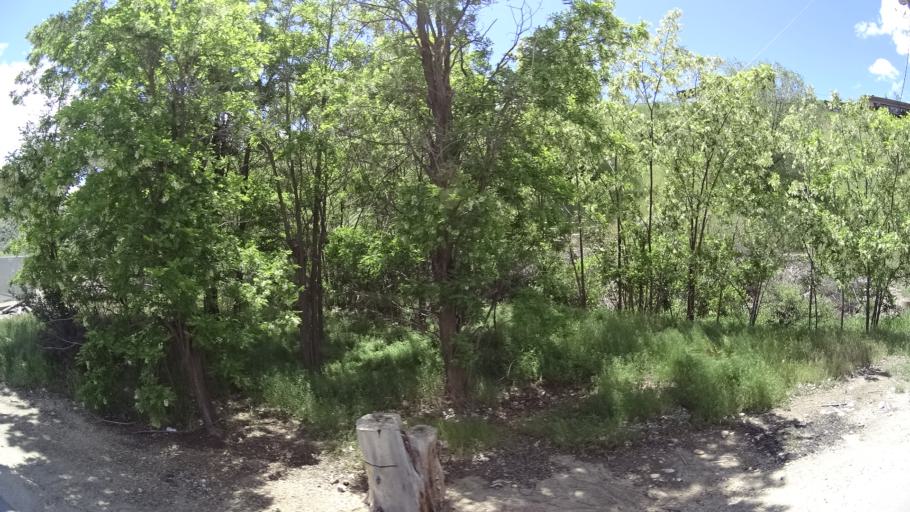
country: US
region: Idaho
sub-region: Ada County
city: Eagle
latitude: 43.6629
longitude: -116.3271
